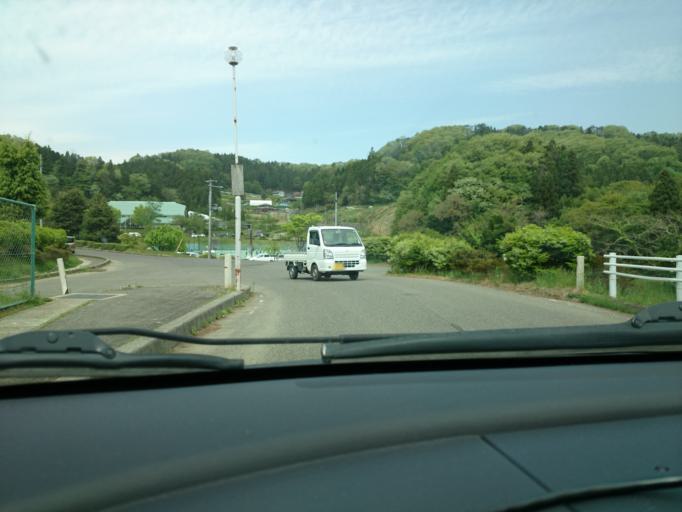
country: JP
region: Fukushima
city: Nihommatsu
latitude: 37.6027
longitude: 140.4319
